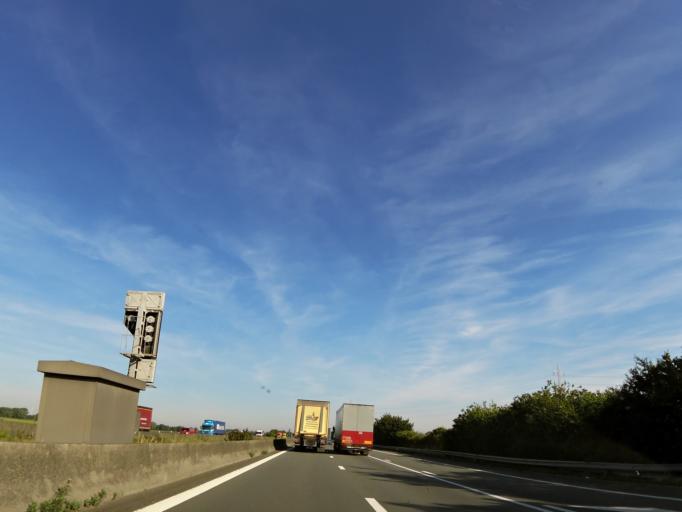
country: BE
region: Flanders
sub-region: Provincie Antwerpen
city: Stabroek
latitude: 51.3298
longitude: 4.3491
